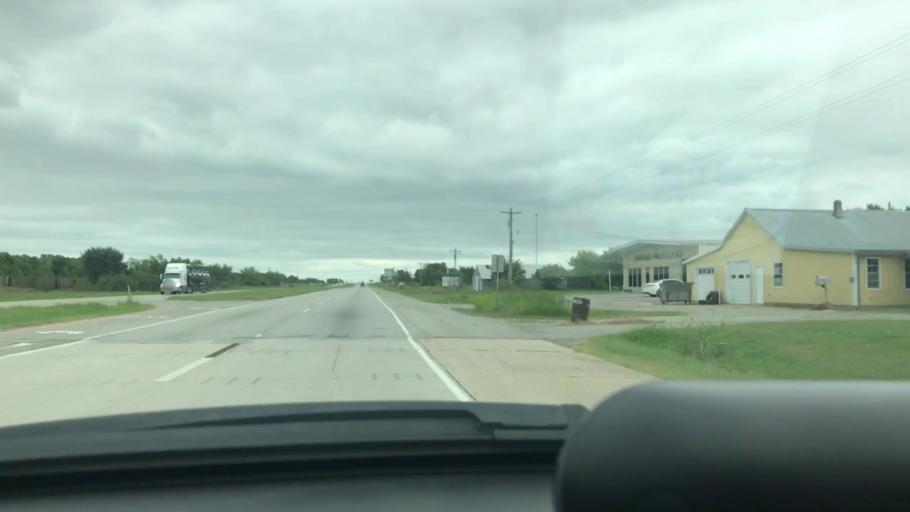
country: US
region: Oklahoma
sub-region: Mayes County
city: Chouteau
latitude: 36.0997
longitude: -95.3626
